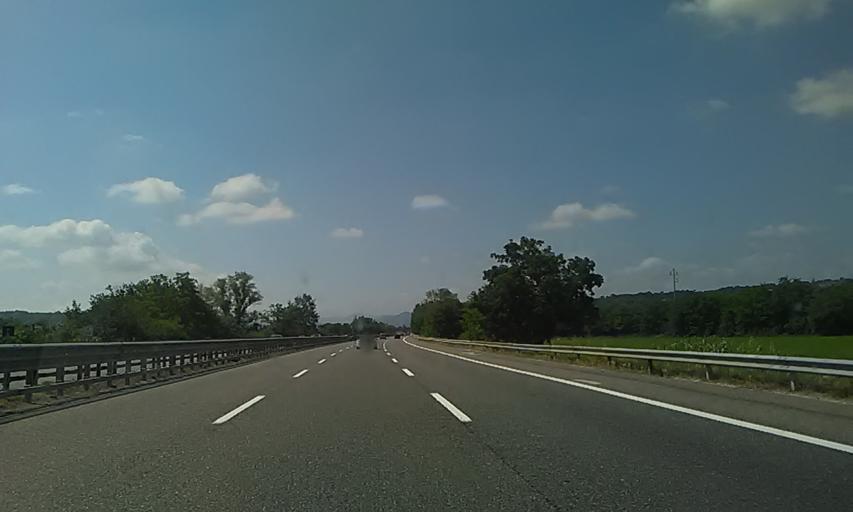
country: IT
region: Piedmont
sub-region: Provincia di Alessandria
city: Silvano d'Orba
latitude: 44.7043
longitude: 8.6674
